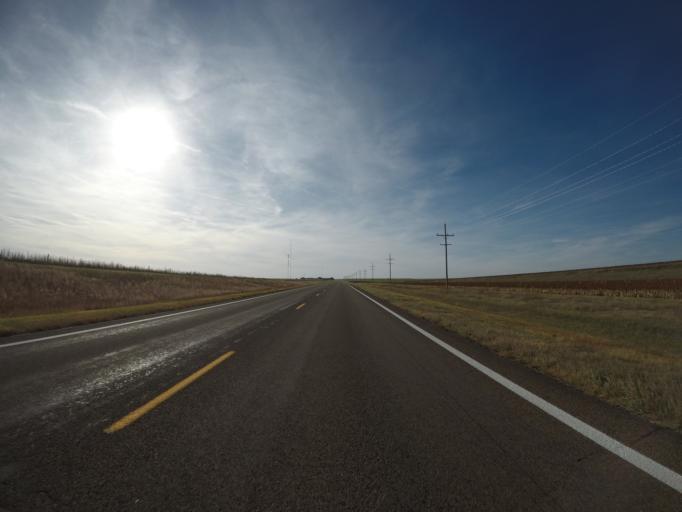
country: US
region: Kansas
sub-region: Rawlins County
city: Atwood
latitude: 39.7854
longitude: -101.2548
